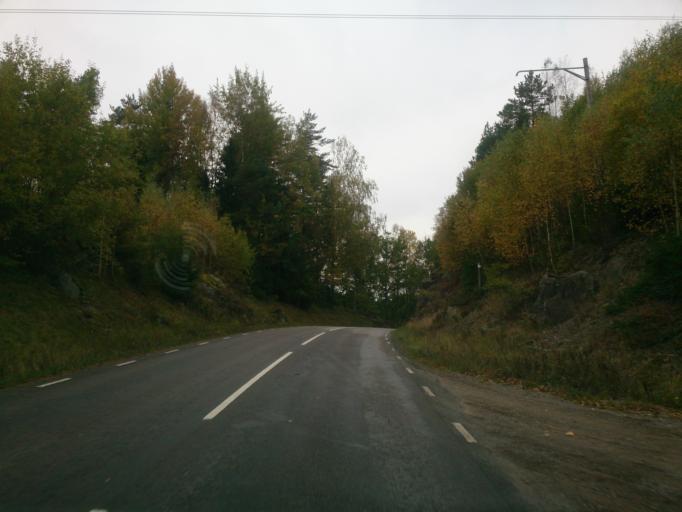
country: SE
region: OEstergoetland
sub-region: Atvidabergs Kommun
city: Atvidaberg
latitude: 58.1788
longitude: 16.0676
